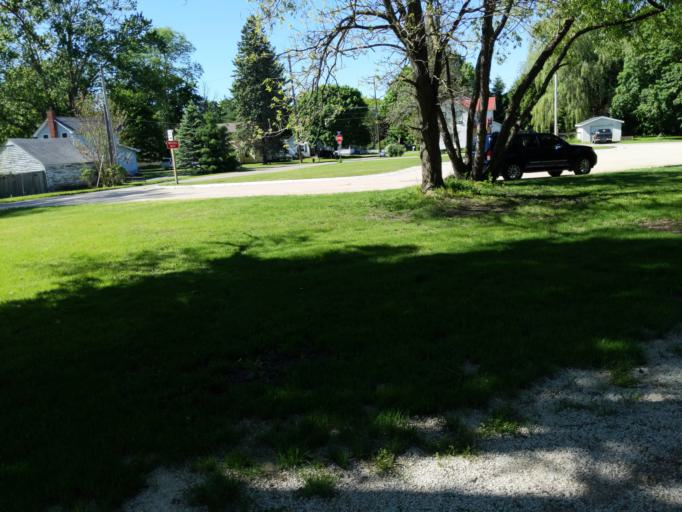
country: US
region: Michigan
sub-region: Ingham County
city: Stockbridge
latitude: 42.4460
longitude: -84.1786
